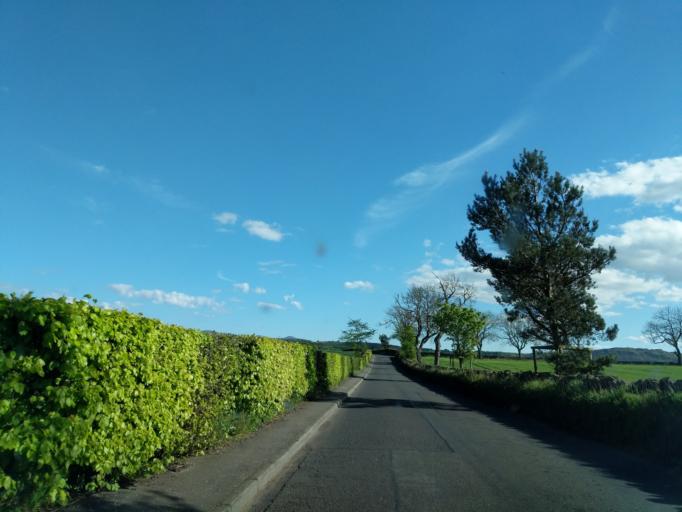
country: GB
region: Scotland
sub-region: Edinburgh
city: Ratho
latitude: 55.9136
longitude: -3.3734
